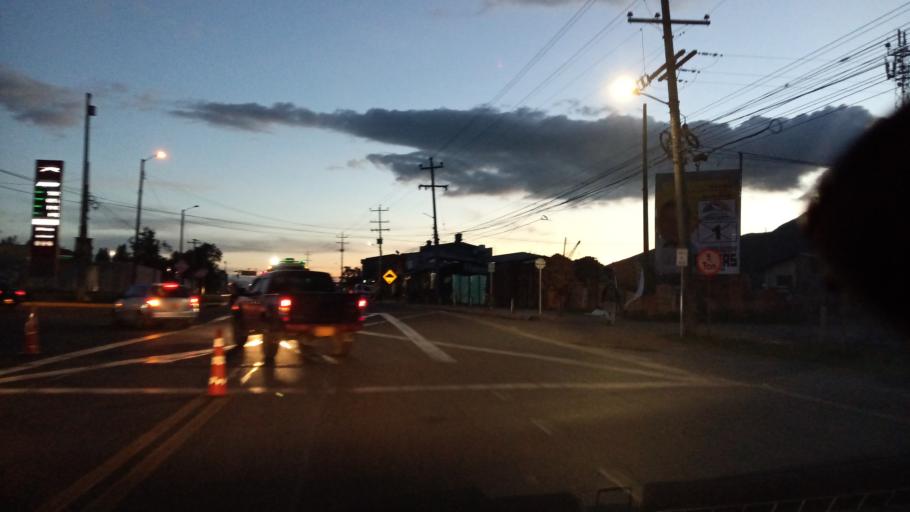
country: CO
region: Cundinamarca
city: Cota
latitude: 4.8267
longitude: -74.0914
